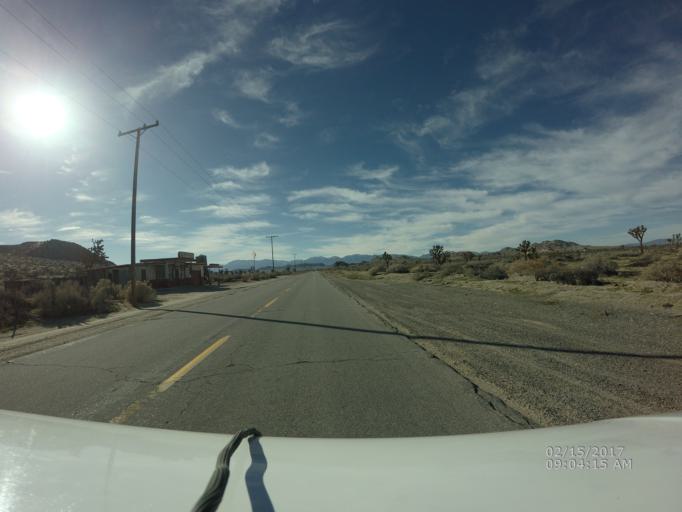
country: US
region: California
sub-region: Los Angeles County
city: Lake Los Angeles
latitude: 34.6616
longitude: -117.8630
